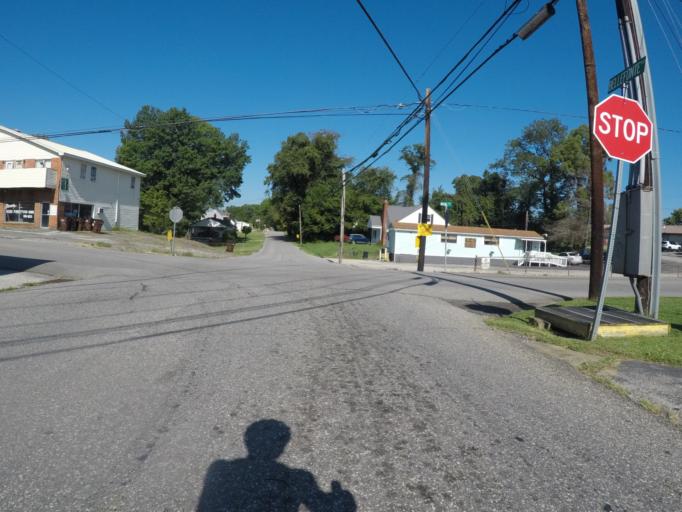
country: US
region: Kentucky
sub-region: Boyd County
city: Westwood
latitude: 38.4835
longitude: -82.6721
